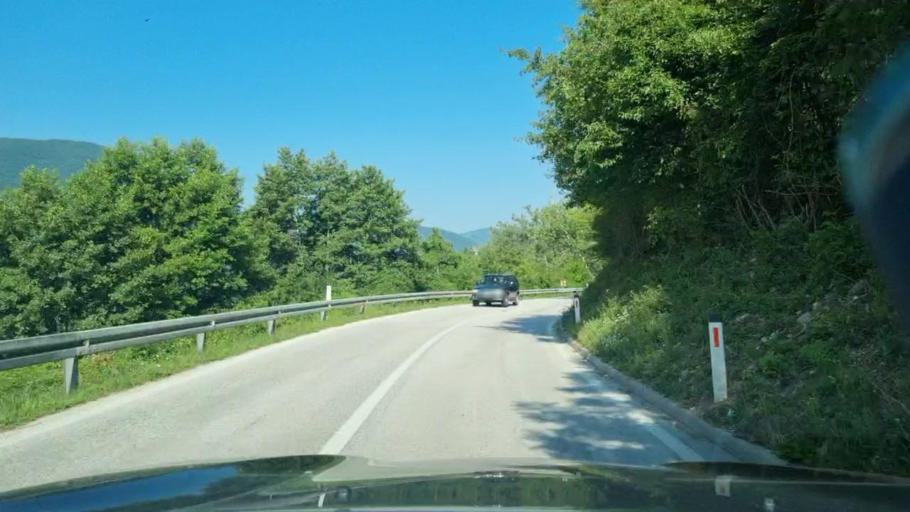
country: BA
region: Federation of Bosnia and Herzegovina
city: Jajce
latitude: 44.3450
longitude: 17.2159
